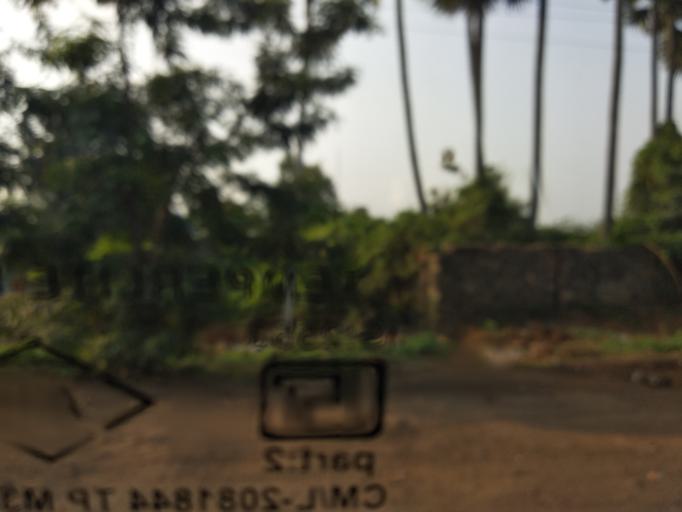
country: IN
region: Andhra Pradesh
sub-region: Vishakhapatnam
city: Visakhapatnam
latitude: 17.6847
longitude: 83.1578
